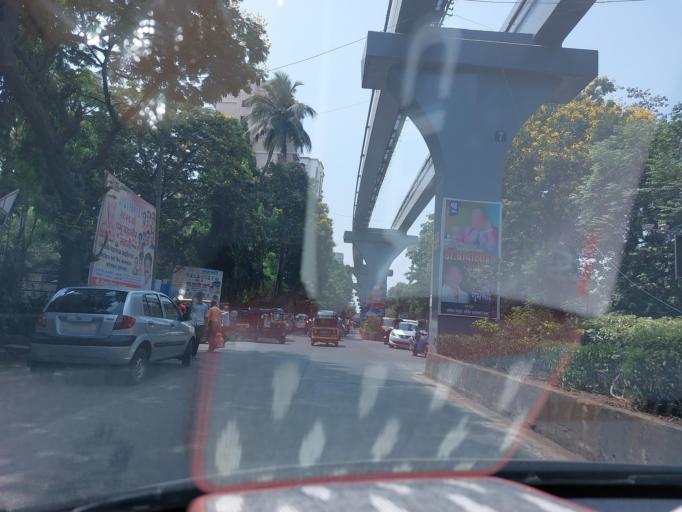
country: IN
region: Maharashtra
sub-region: Mumbai Suburban
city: Mumbai
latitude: 19.0570
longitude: 72.8953
